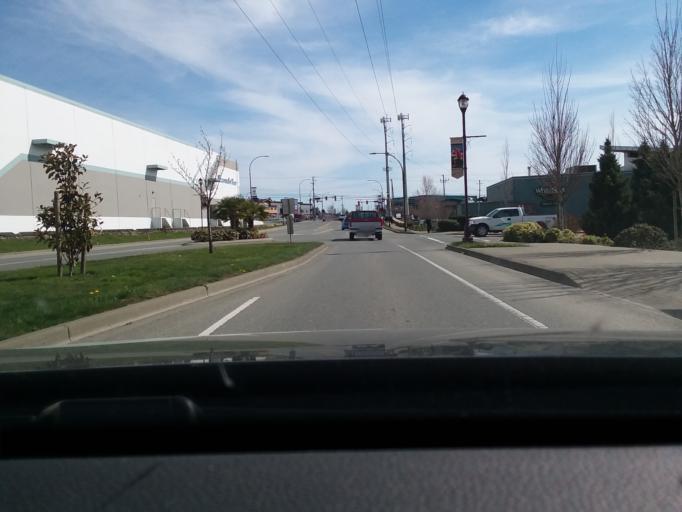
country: CA
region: British Columbia
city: Langford
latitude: 48.4428
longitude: -123.5130
